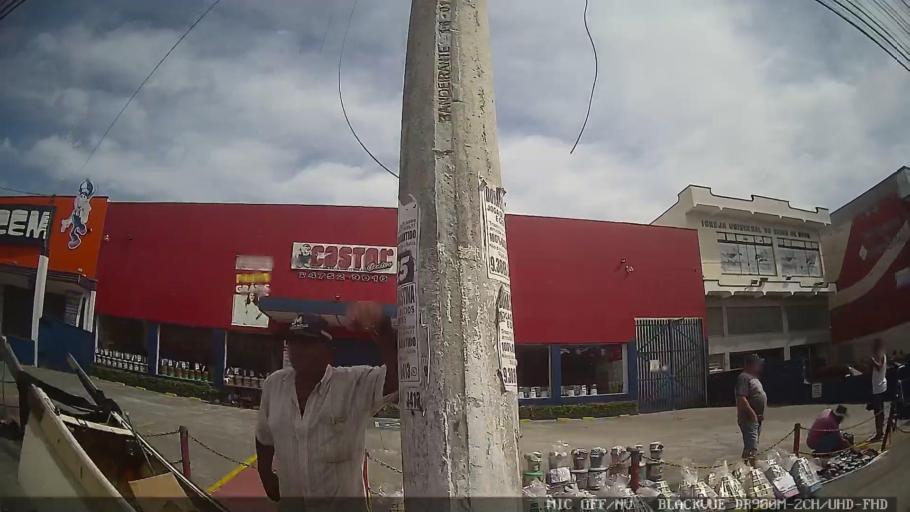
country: BR
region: Sao Paulo
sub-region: Suzano
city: Suzano
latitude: -23.5017
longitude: -46.2987
